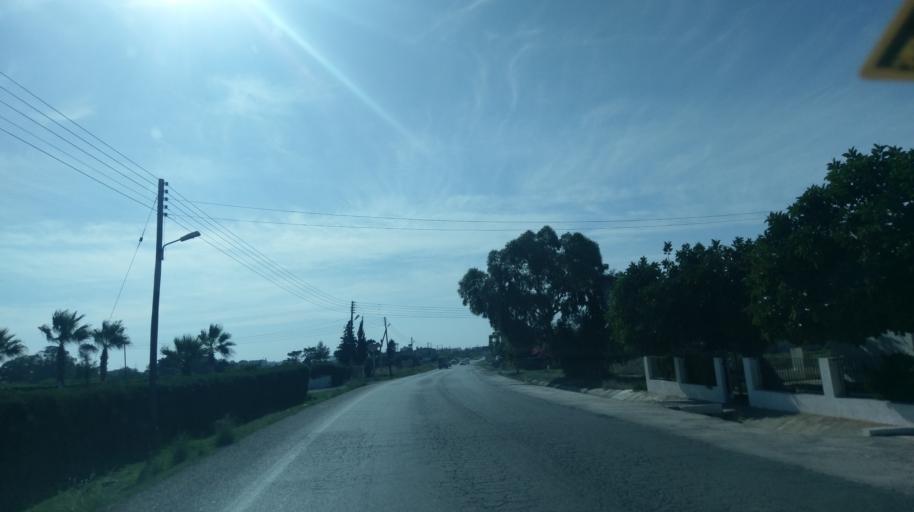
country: CY
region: Ammochostos
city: Trikomo
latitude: 35.2894
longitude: 33.9310
